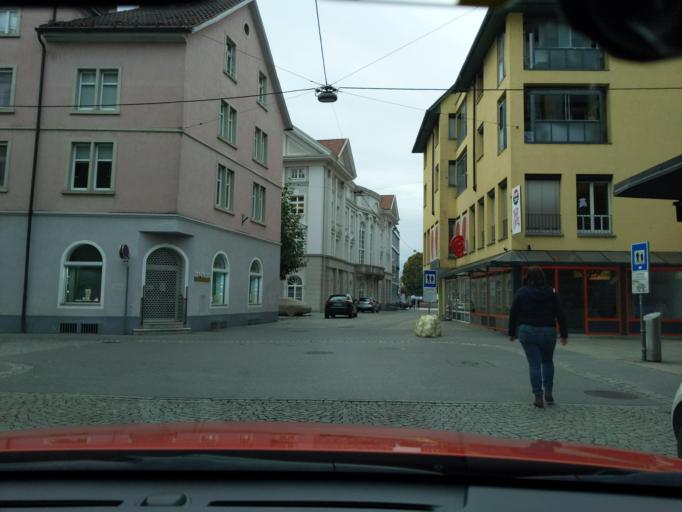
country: AT
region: Vorarlberg
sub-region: Politischer Bezirk Bregenz
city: Bregenz
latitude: 47.5030
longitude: 9.7453
